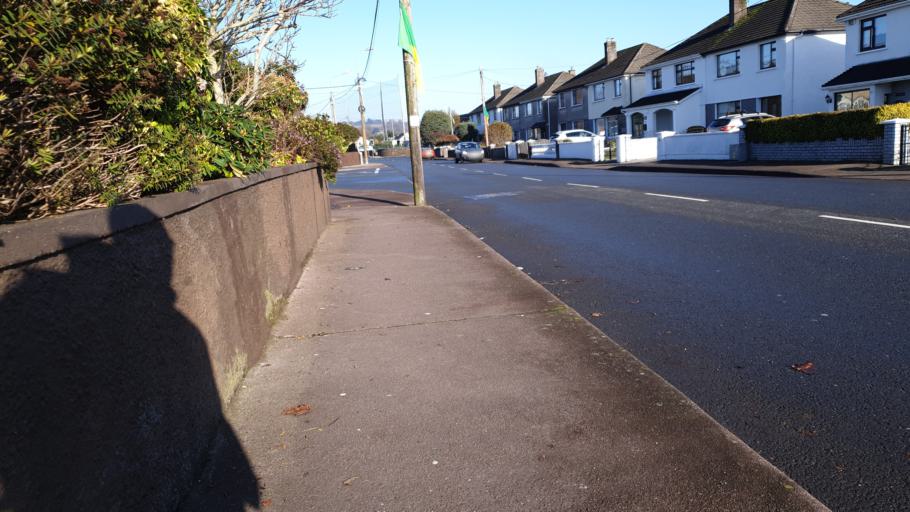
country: IE
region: Munster
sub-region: County Cork
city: Cork
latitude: 51.8912
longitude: -8.4197
